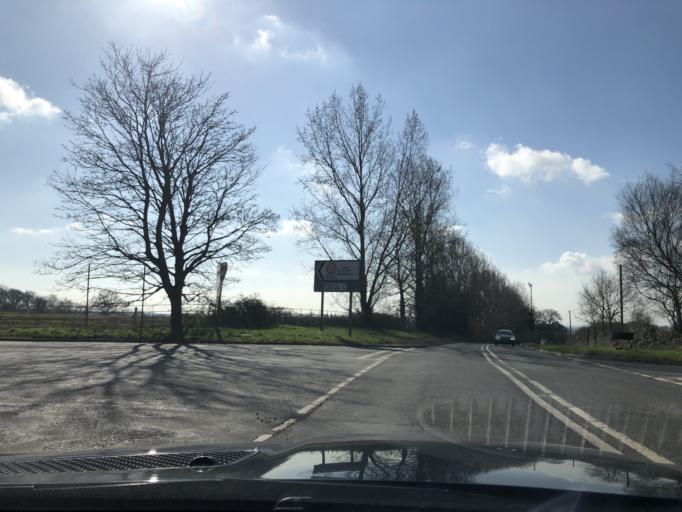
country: GB
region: England
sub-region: Warwickshire
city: Harbury
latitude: 52.2873
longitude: -1.4541
